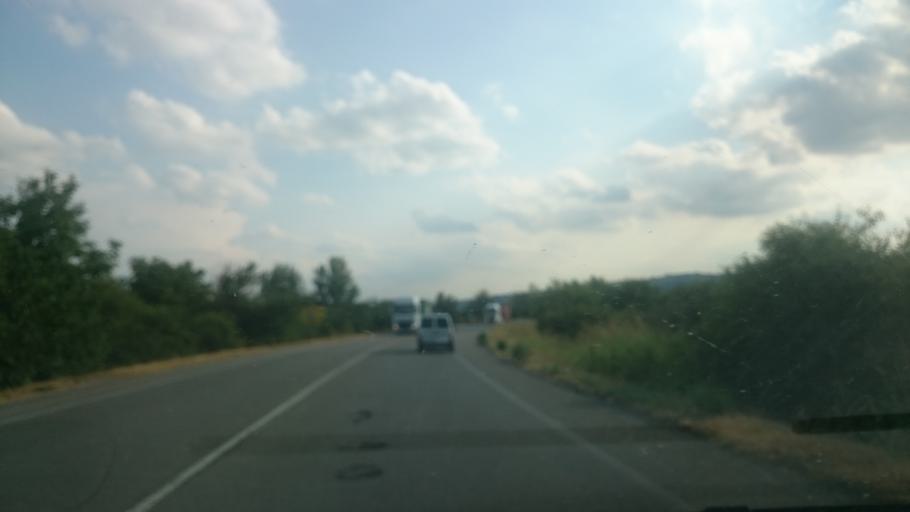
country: IT
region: Emilia-Romagna
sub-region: Provincia di Reggio Emilia
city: Salvaterra
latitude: 44.5926
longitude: 10.7742
